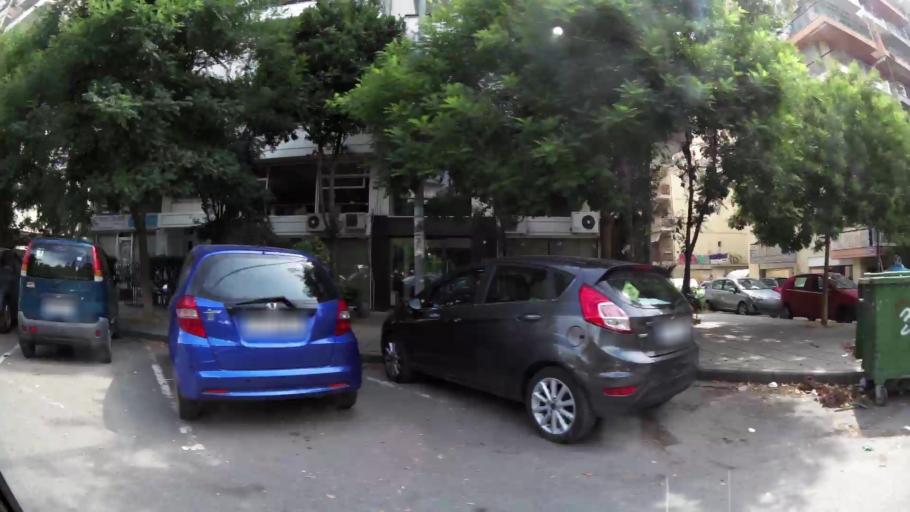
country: GR
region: Central Macedonia
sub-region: Nomos Thessalonikis
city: Kalamaria
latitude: 40.5975
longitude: 22.9613
